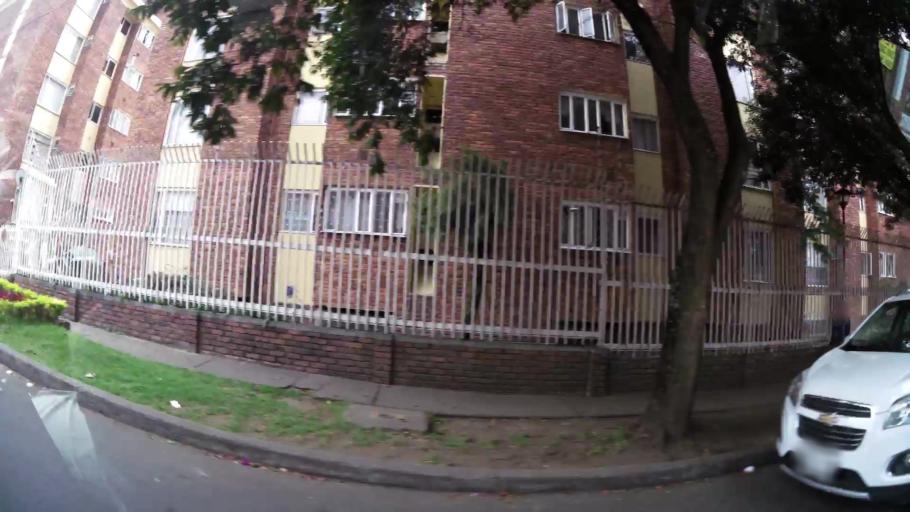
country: CO
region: Bogota D.C.
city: Barrio San Luis
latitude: 4.6865
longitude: -74.0721
